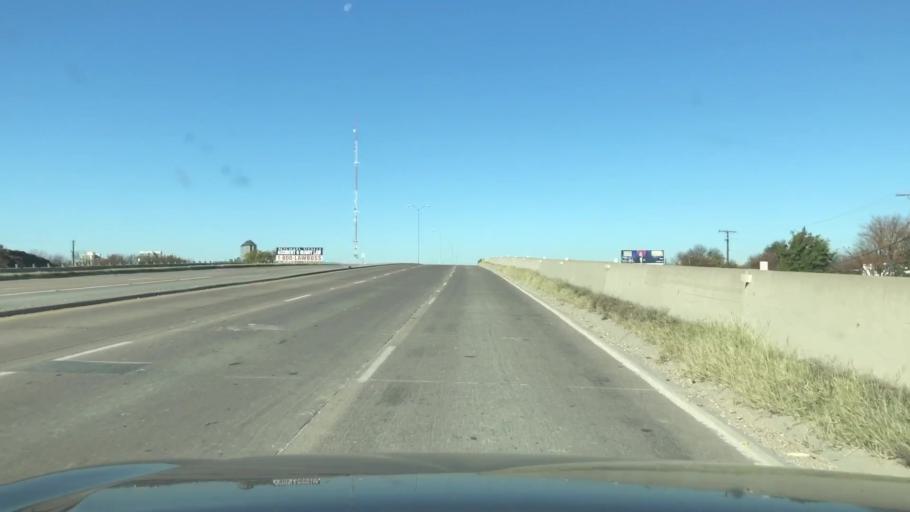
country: US
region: Texas
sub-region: Dallas County
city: Farmers Branch
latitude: 32.8693
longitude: -96.9139
